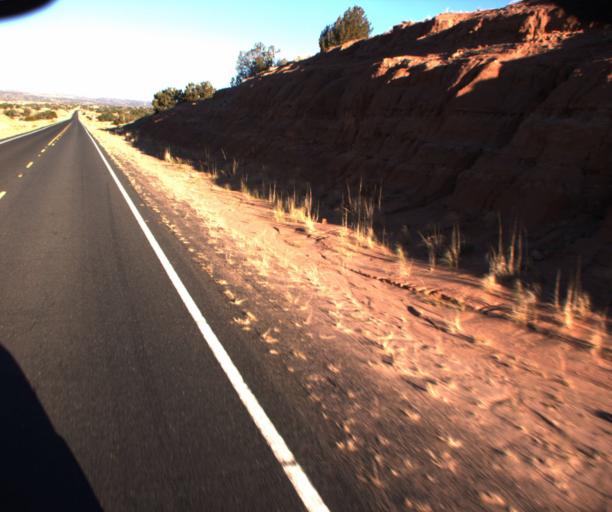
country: US
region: Arizona
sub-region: Apache County
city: Houck
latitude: 35.3692
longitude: -109.4779
